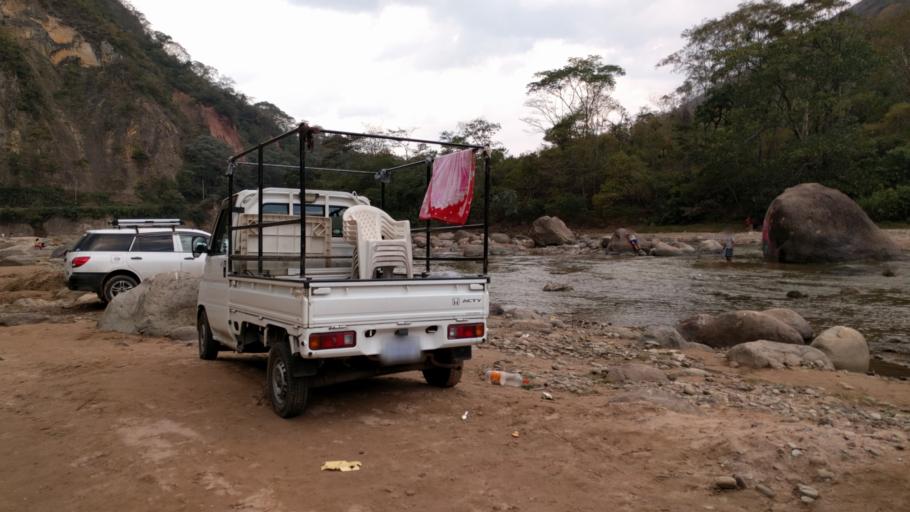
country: BO
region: Santa Cruz
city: Jorochito
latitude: -18.1689
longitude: -63.5268
